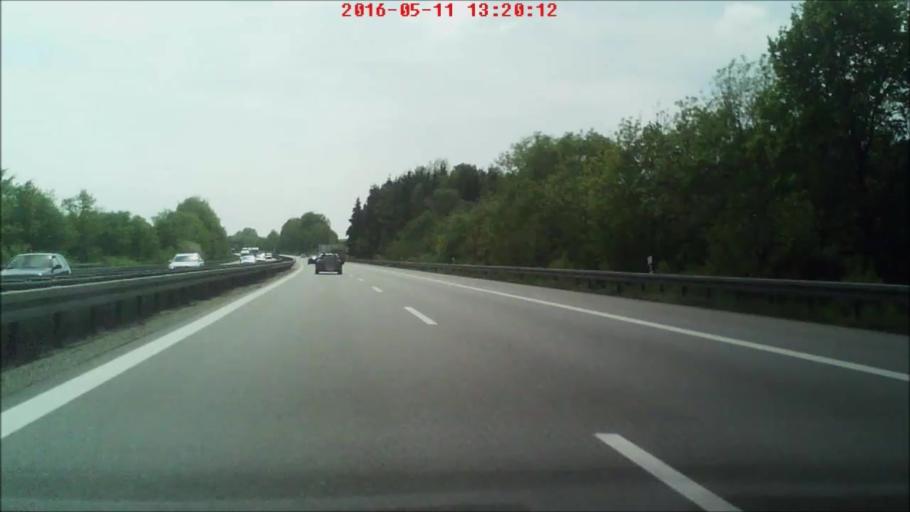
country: DE
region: Bavaria
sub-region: Lower Bavaria
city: Furstenzell
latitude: 48.5029
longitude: 13.3834
